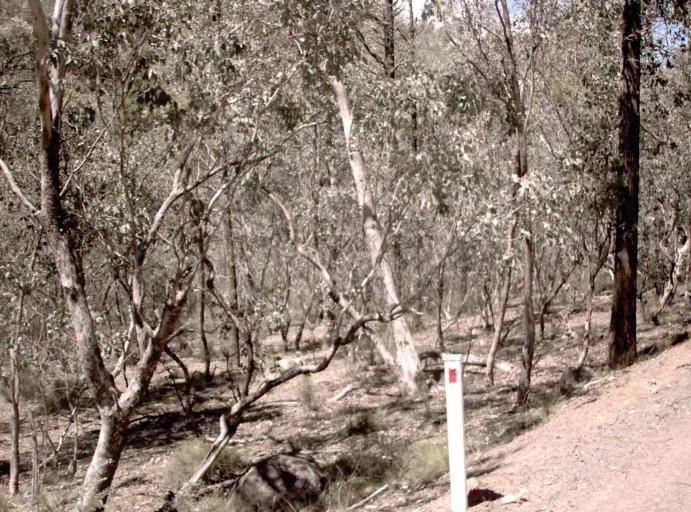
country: AU
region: New South Wales
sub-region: Snowy River
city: Jindabyne
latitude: -37.0633
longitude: 148.5100
